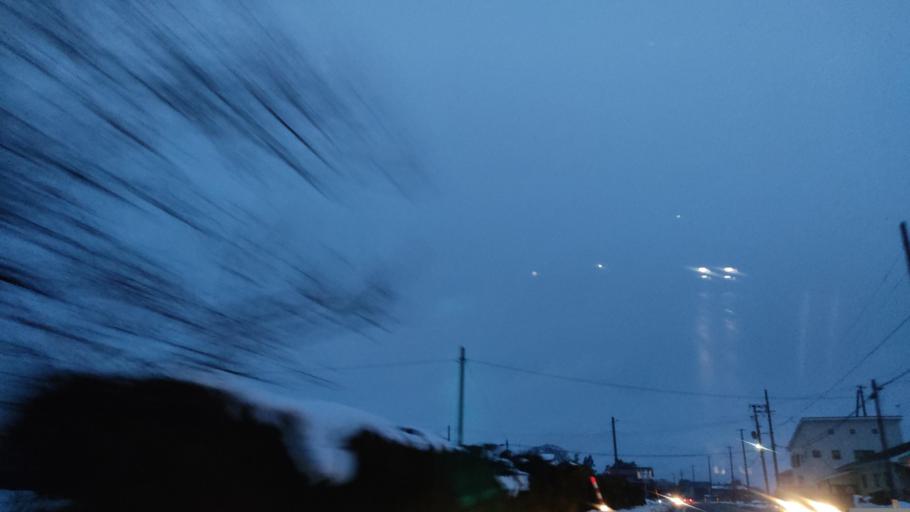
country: JP
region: Iwate
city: Morioka-shi
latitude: 39.6117
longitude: 141.1135
